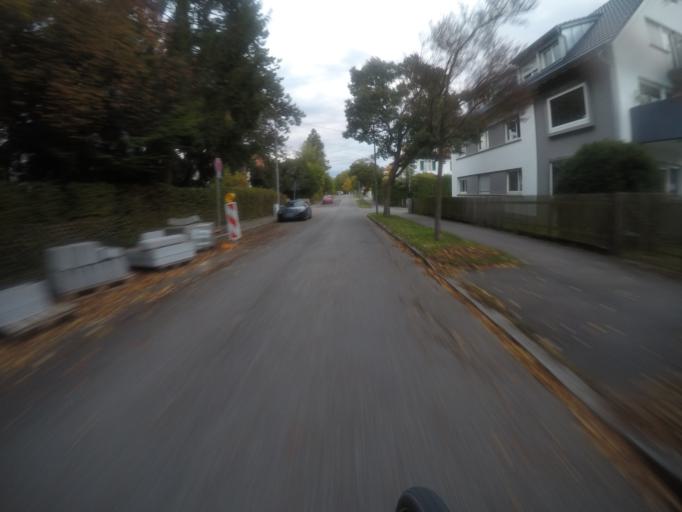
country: DE
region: Baden-Wuerttemberg
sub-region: Regierungsbezirk Stuttgart
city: Steinenbronn
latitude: 48.7179
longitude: 9.0974
